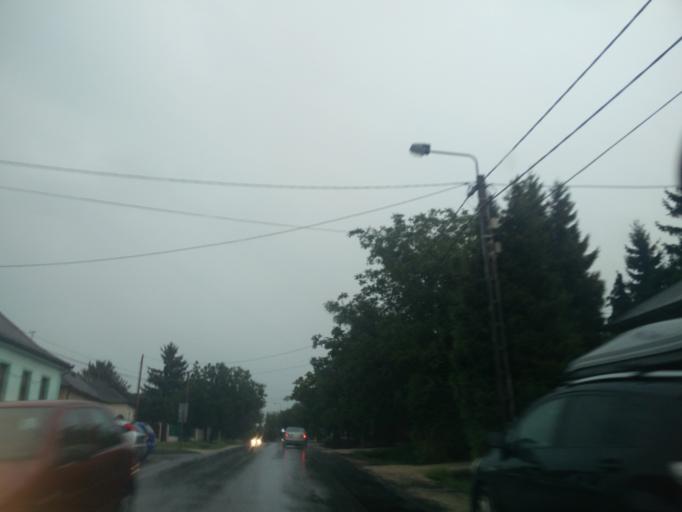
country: HU
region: Pest
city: Biatorbagy
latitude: 47.4673
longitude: 18.8165
